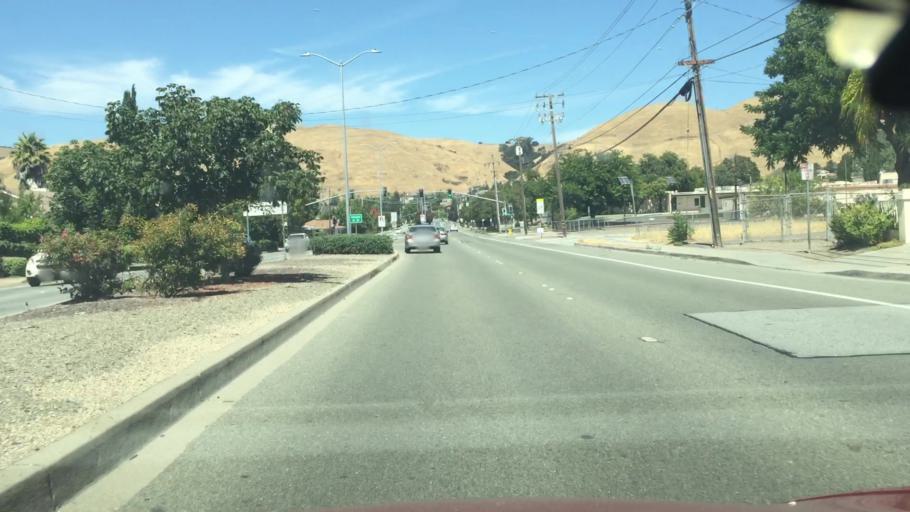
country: US
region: California
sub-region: Alameda County
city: Fremont
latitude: 37.5456
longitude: -121.9440
